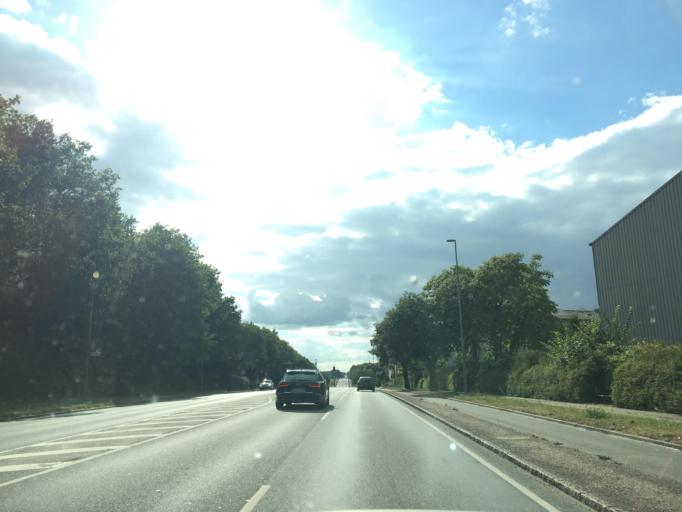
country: DK
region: South Denmark
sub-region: Odense Kommune
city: Odense
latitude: 55.3932
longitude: 10.3322
